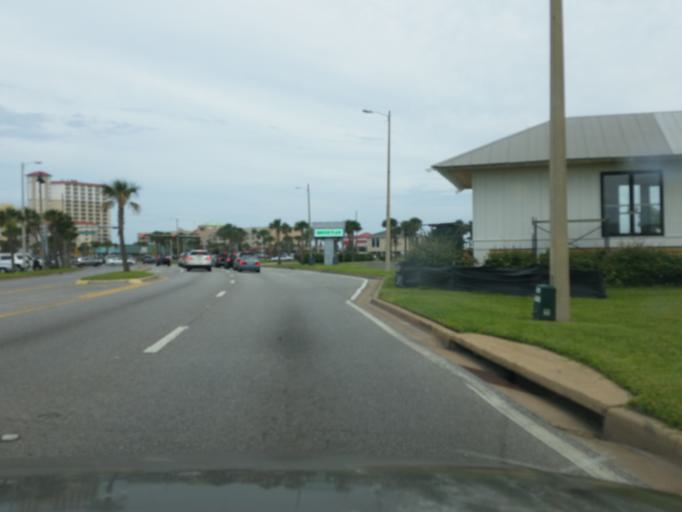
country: US
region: Florida
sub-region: Santa Rosa County
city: Gulf Breeze
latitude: 30.3343
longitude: -87.1425
